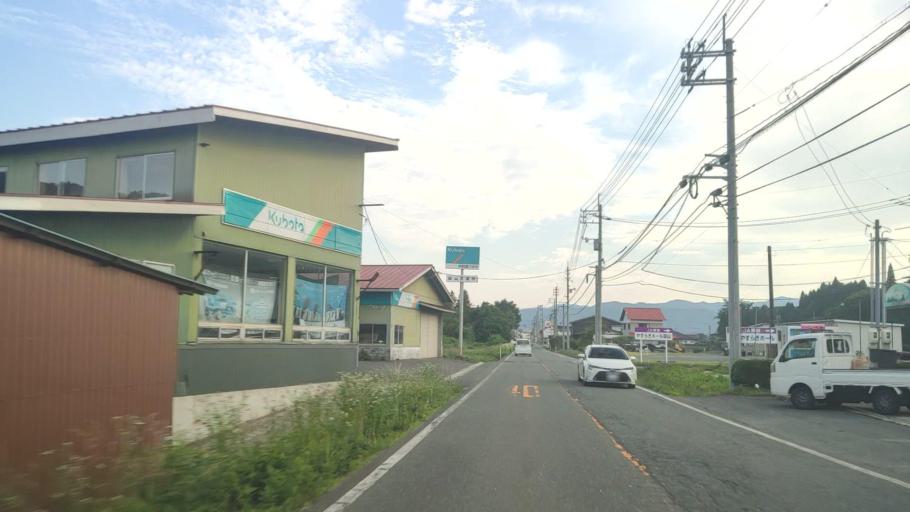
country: JP
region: Tottori
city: Kurayoshi
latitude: 35.2865
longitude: 133.6994
